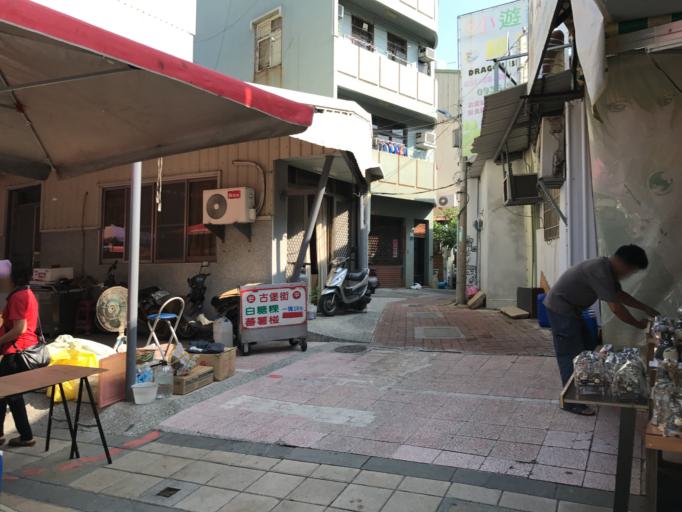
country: TW
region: Taiwan
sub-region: Tainan
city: Tainan
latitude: 23.0017
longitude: 120.1614
